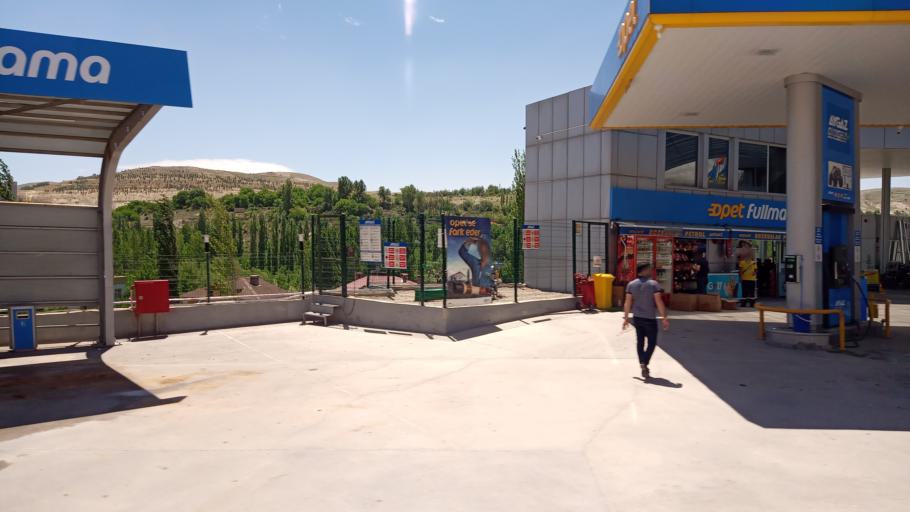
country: TR
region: Sivas
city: Gurun
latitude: 38.7222
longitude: 37.2808
